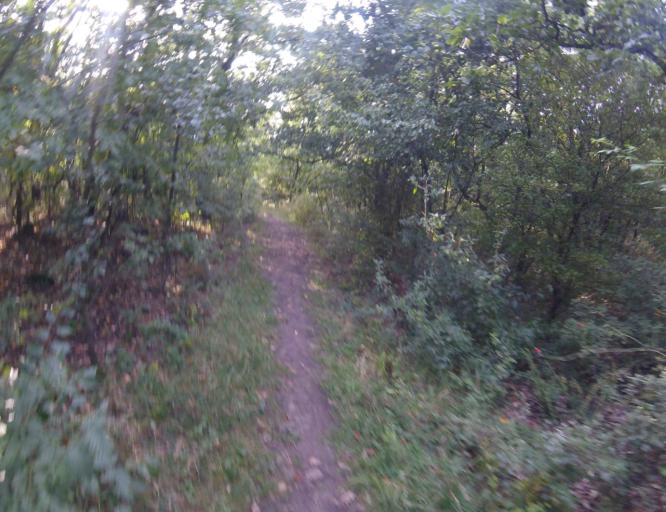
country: HU
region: Pest
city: Nagykovacsi
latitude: 47.6779
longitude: 19.0161
